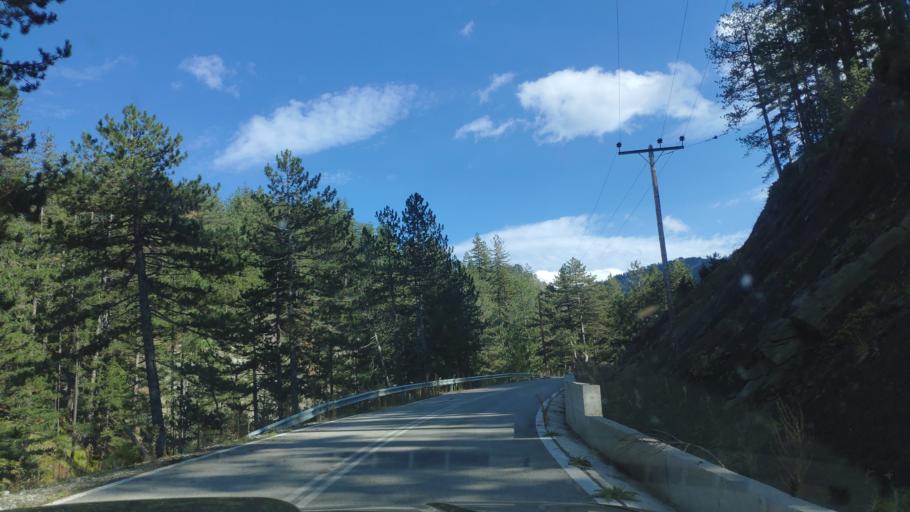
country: AL
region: Korce
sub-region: Rrethi i Devollit
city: Miras
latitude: 40.4050
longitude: 20.8783
